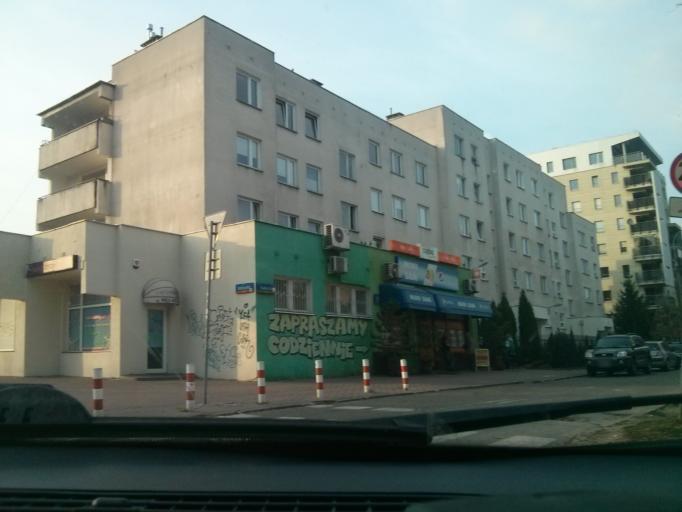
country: PL
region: Masovian Voivodeship
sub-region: Warszawa
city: Mokotow
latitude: 52.1735
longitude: 21.0300
